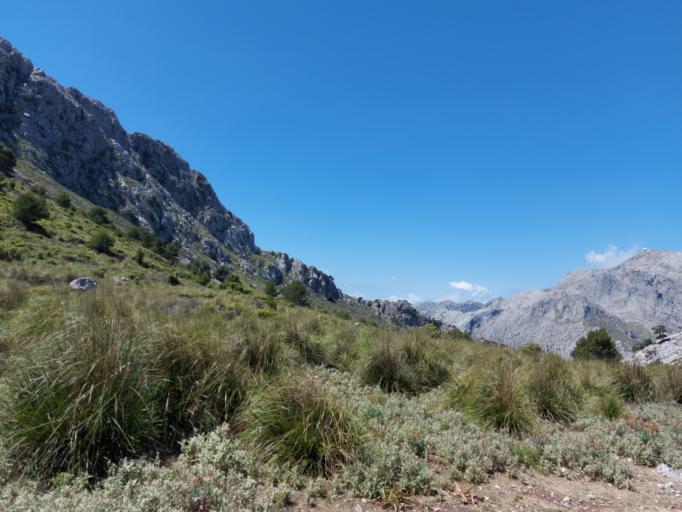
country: ES
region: Balearic Islands
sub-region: Illes Balears
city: Escorca
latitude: 39.8119
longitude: 2.8413
